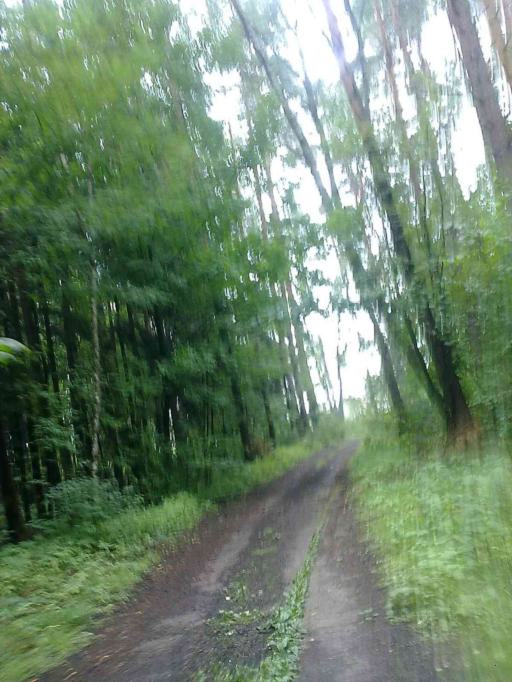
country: RU
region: Moskovskaya
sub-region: Leninskiy Rayon
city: Vnukovo
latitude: 55.6360
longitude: 37.3027
